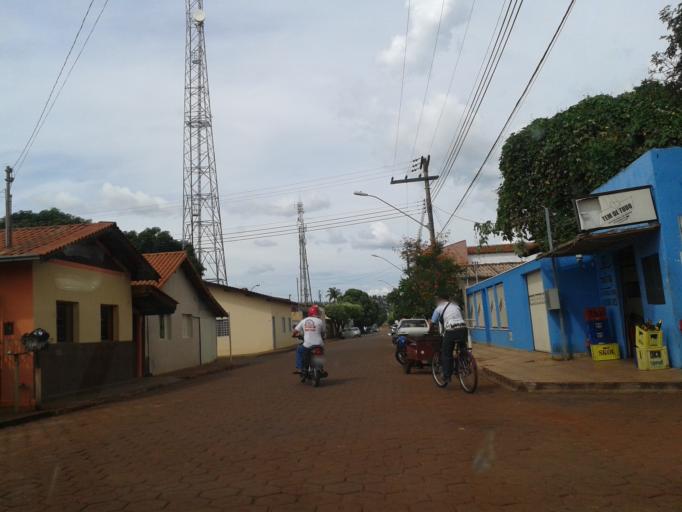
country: BR
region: Minas Gerais
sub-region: Centralina
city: Centralina
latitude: -18.5865
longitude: -49.1998
